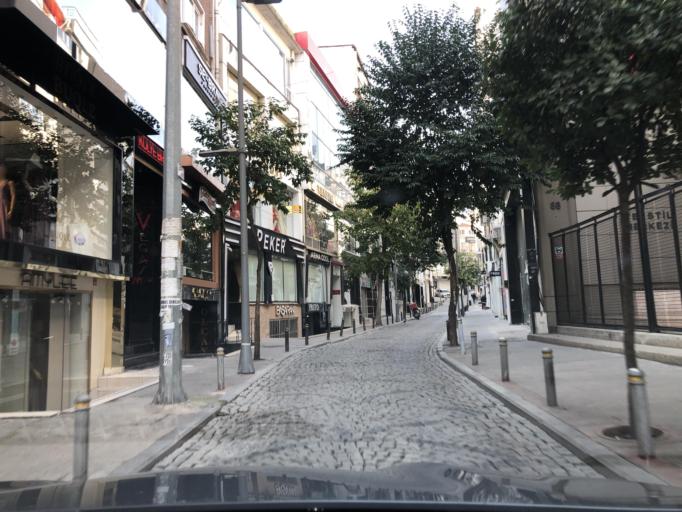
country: TR
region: Istanbul
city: Sisli
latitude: 41.0544
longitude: 28.9906
